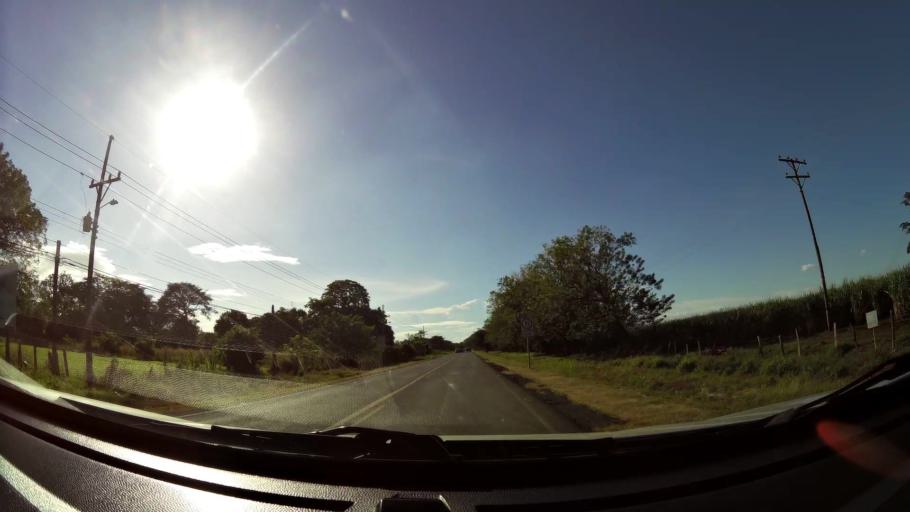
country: CR
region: Guanacaste
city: Belen
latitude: 10.4857
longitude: -85.5673
